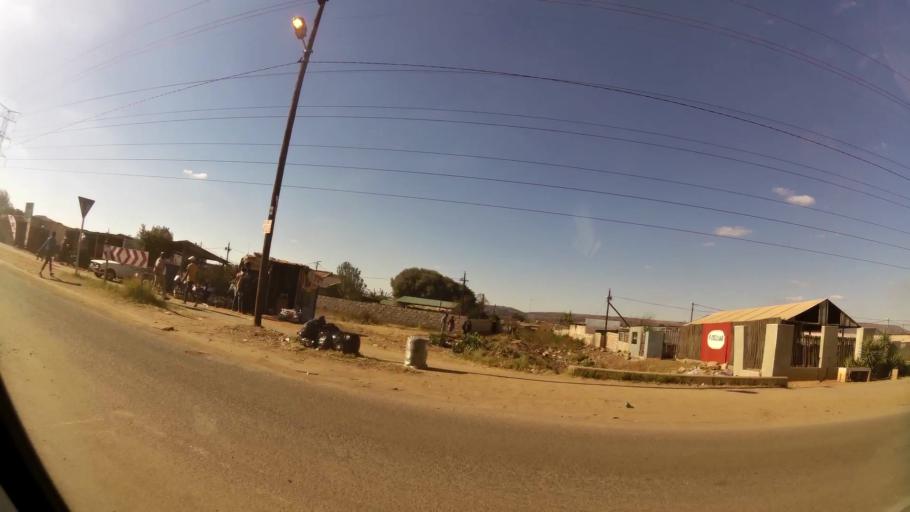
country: ZA
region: Gauteng
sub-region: City of Tshwane Metropolitan Municipality
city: Cullinan
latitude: -25.7082
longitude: 28.3962
